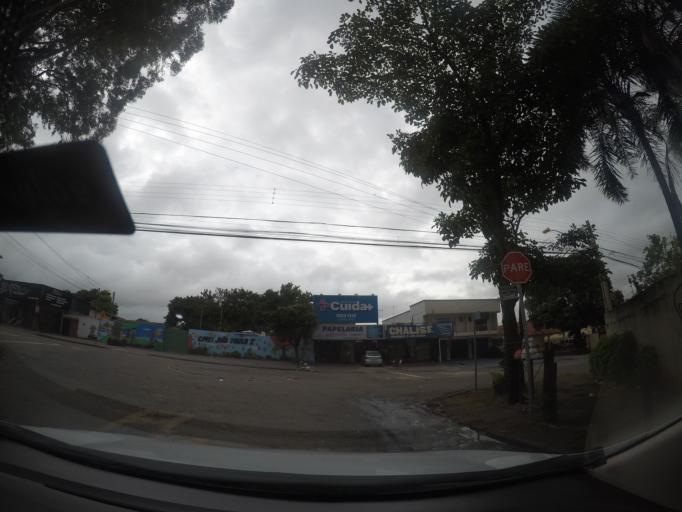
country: BR
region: Goias
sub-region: Goiania
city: Goiania
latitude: -16.7213
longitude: -49.2894
